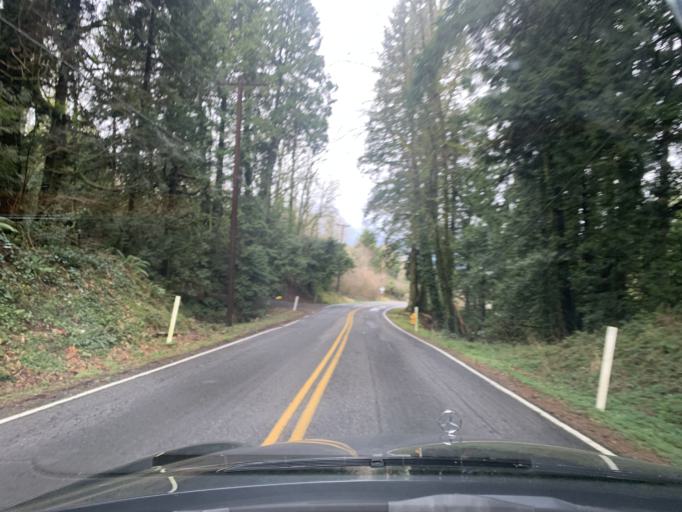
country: US
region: Oregon
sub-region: Multnomah County
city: Gresham
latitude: 45.4748
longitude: -122.4298
